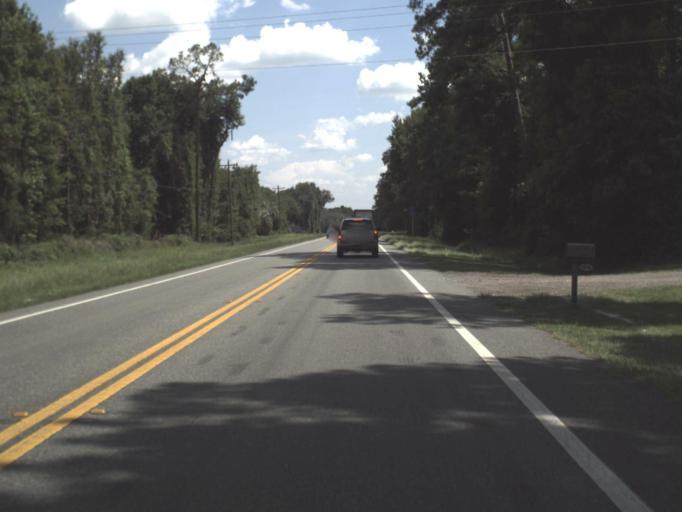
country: US
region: Florida
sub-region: Columbia County
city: Watertown
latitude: 30.0316
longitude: -82.5977
